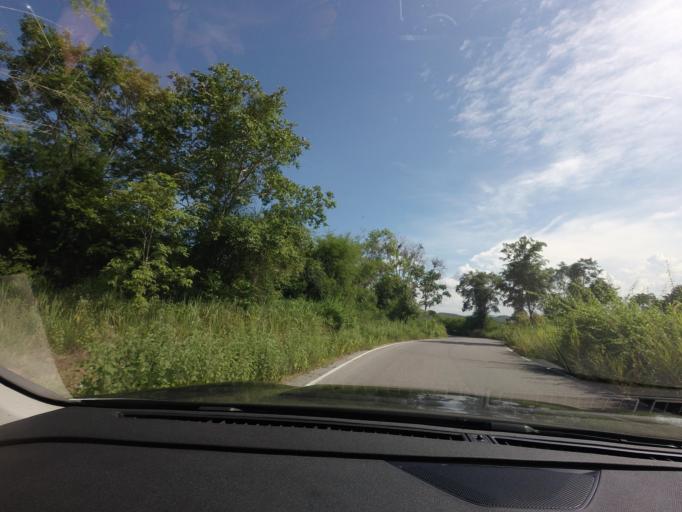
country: TH
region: Prachuap Khiri Khan
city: Hua Hin
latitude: 12.4889
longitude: 99.9424
